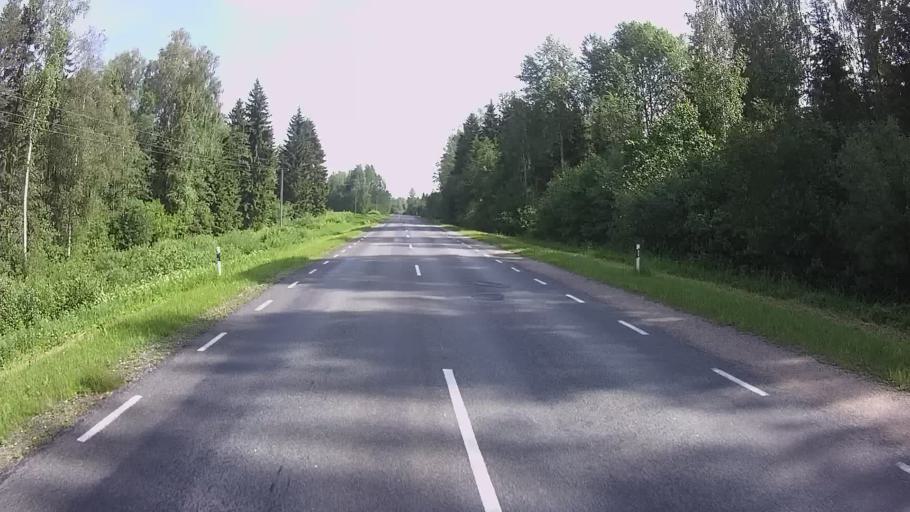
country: EE
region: Tartu
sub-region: Elva linn
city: Elva
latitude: 57.9943
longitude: 26.2654
